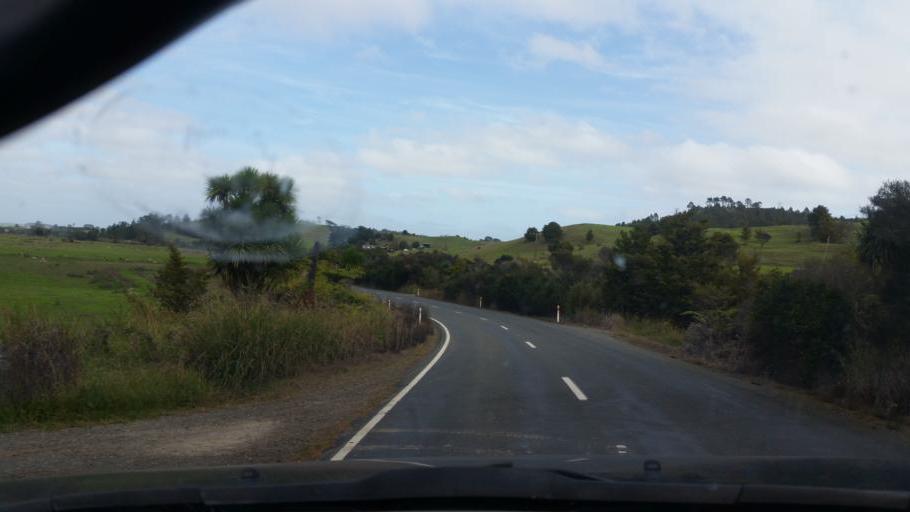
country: NZ
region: Northland
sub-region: Kaipara District
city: Dargaville
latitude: -35.8822
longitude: 173.8443
